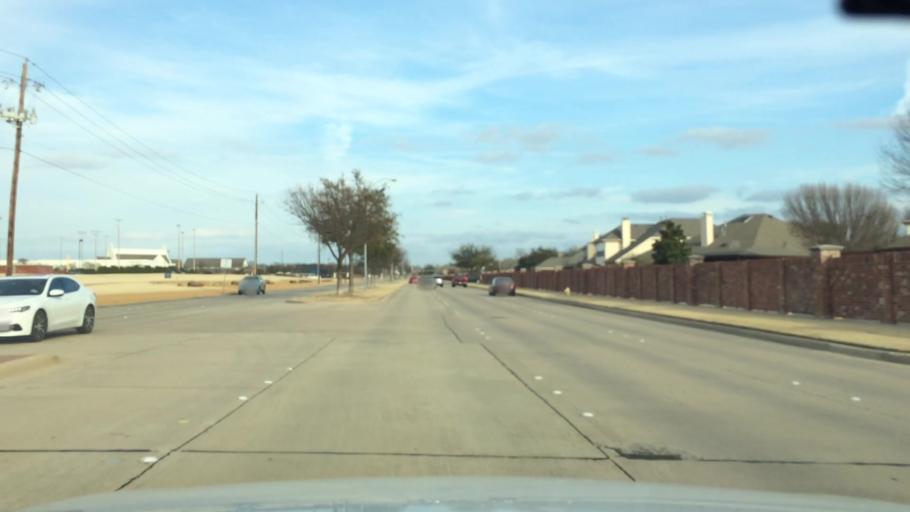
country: US
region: Texas
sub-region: Collin County
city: Frisco
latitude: 33.0861
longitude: -96.7869
